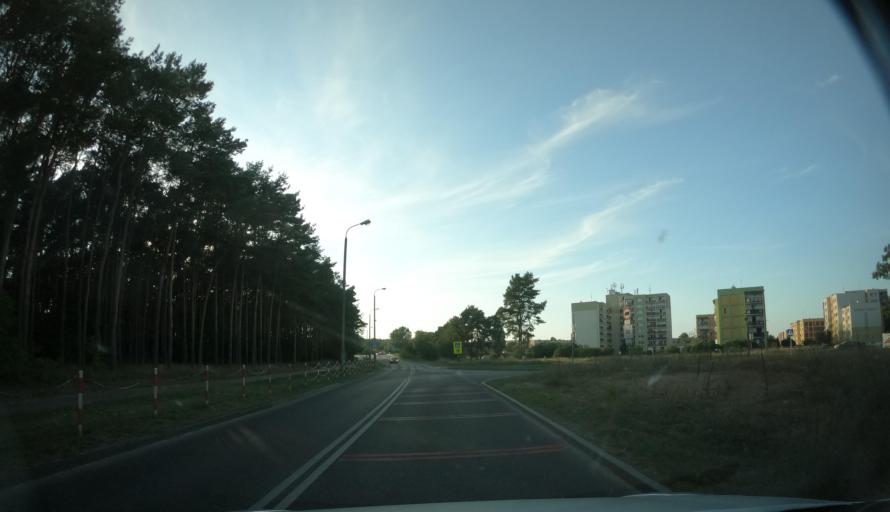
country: PL
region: Kujawsko-Pomorskie
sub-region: Bydgoszcz
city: Fordon
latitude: 53.1529
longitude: 18.1637
